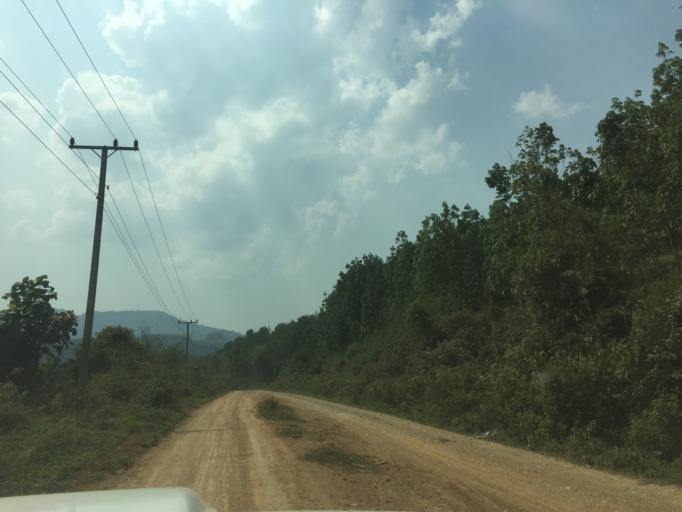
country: TH
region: Nan
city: Thung Chang
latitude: 19.7314
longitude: 100.7381
